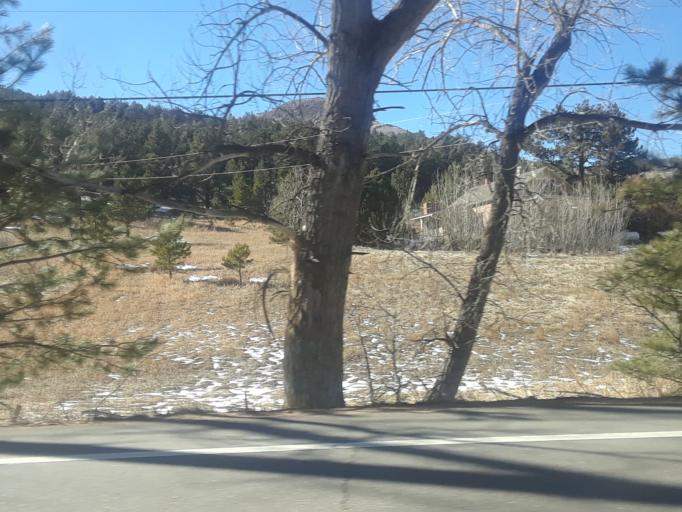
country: US
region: Colorado
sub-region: Boulder County
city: Lyons
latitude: 40.1233
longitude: -105.3063
